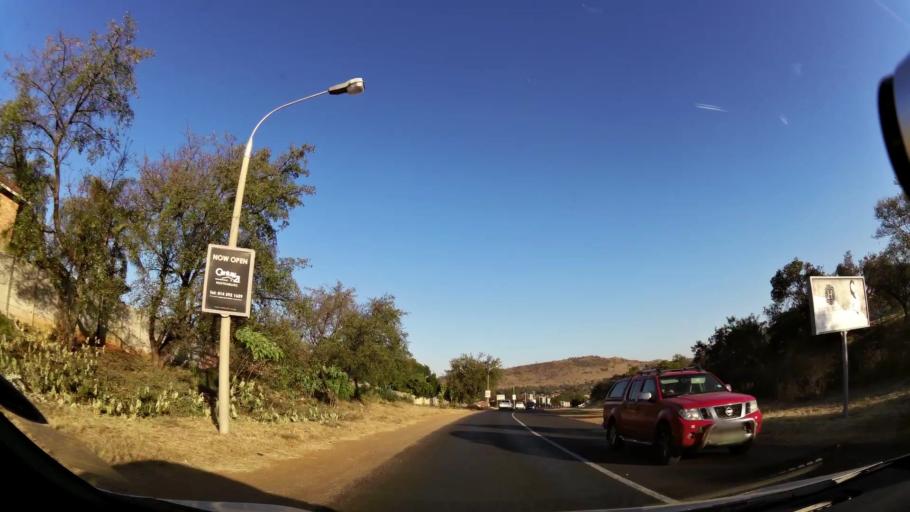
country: ZA
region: North-West
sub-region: Bojanala Platinum District Municipality
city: Rustenburg
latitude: -25.7068
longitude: 27.2395
